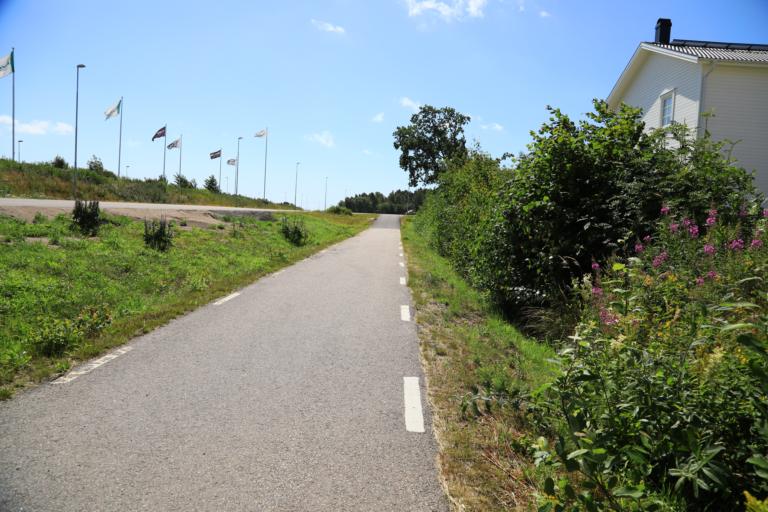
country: SE
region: Halland
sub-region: Varbergs Kommun
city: Traslovslage
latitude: 57.0985
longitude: 12.2940
